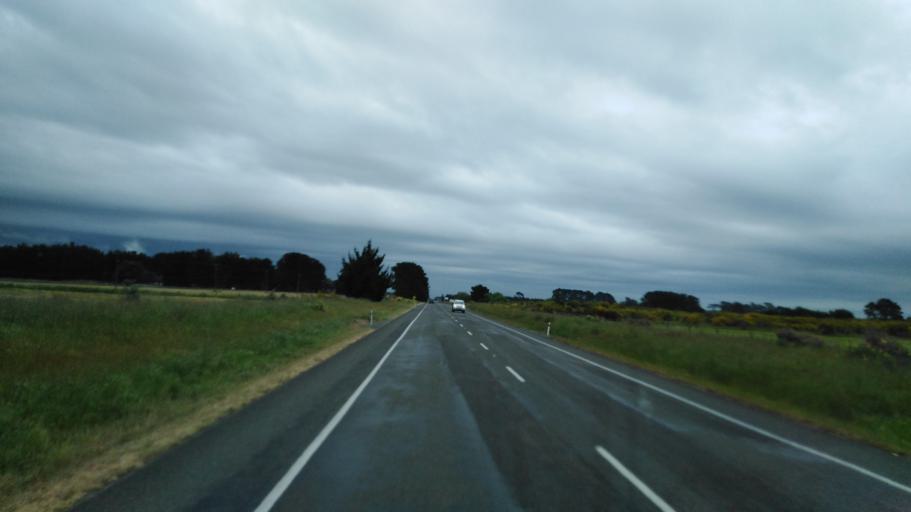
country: NZ
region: Manawatu-Wanganui
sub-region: Horowhenua District
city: Foxton
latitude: -40.4256
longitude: 175.3034
